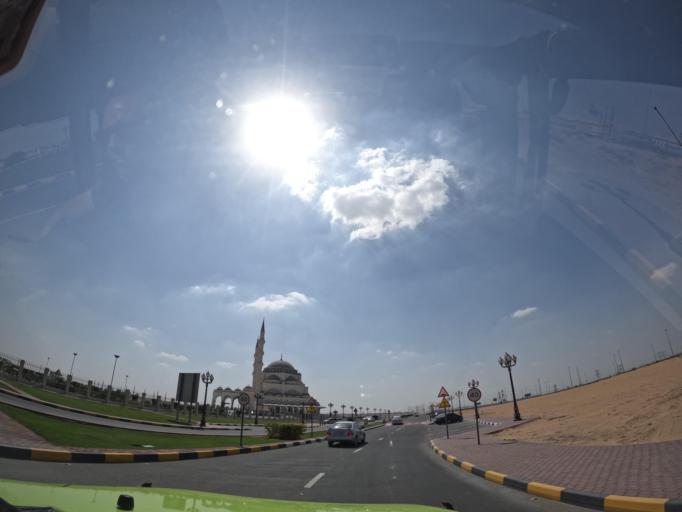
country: AE
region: Ash Shariqah
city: Sharjah
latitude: 25.2432
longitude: 55.5701
